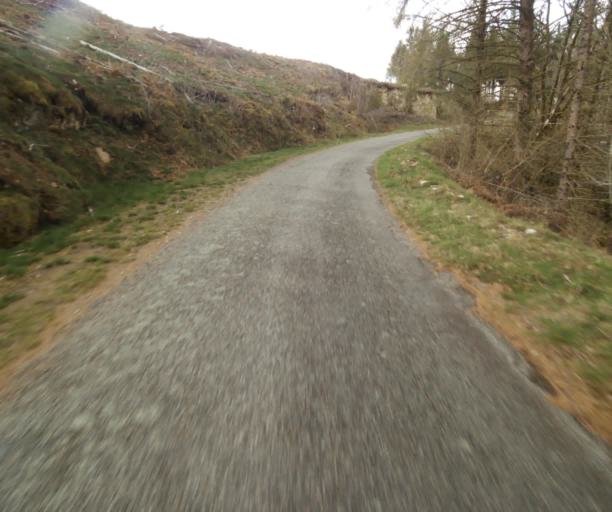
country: FR
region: Limousin
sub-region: Departement de la Correze
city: Egletons
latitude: 45.2748
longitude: 1.9939
